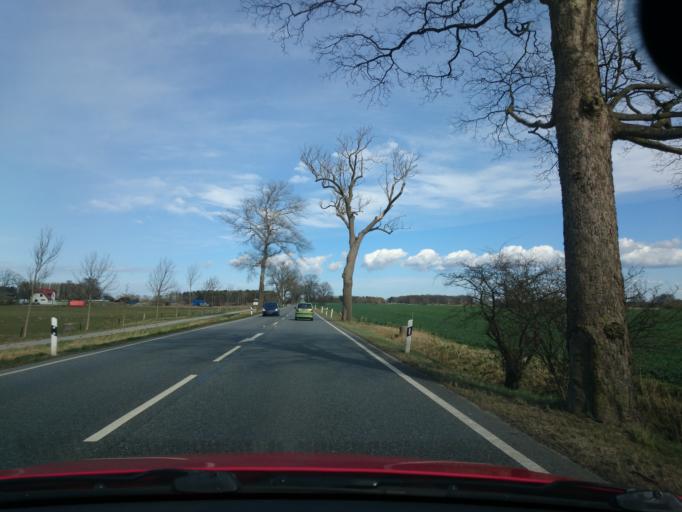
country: DE
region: Mecklenburg-Vorpommern
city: Ostseebad Dierhagen
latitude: 54.2243
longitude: 12.3699
